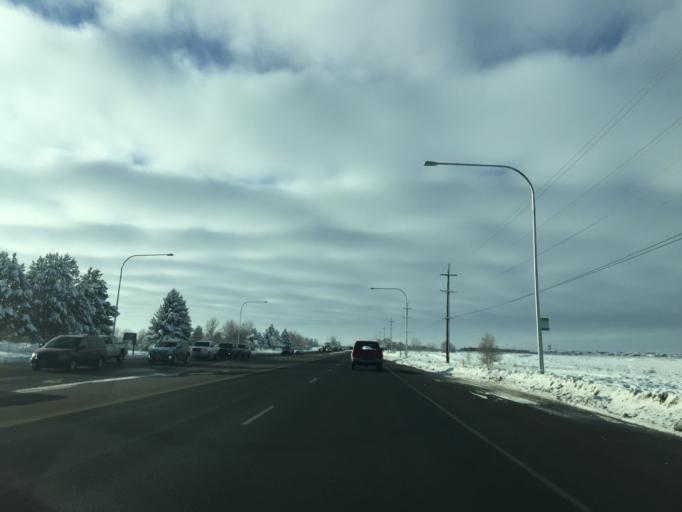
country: US
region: Washington
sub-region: Spokane County
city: Airway Heights
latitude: 47.6433
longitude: -117.5408
